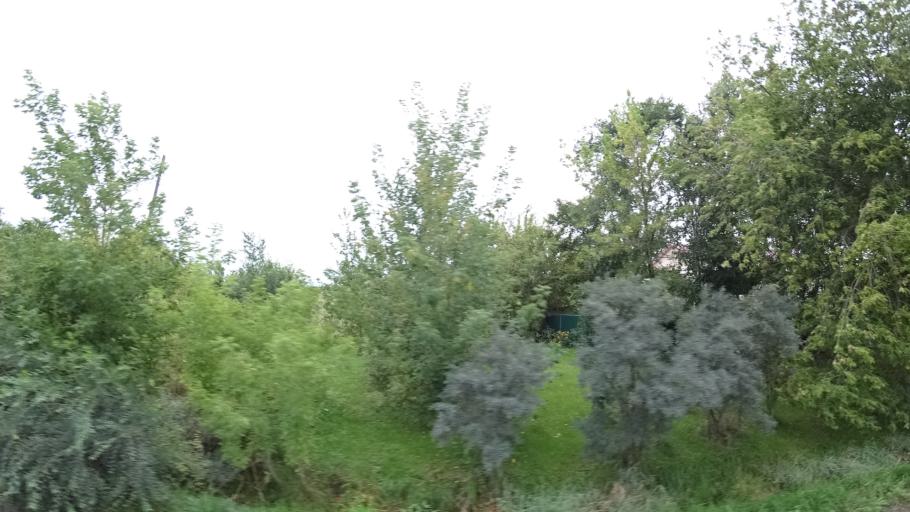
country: RU
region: Primorskiy
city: Chernigovka
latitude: 44.3445
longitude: 132.5560
